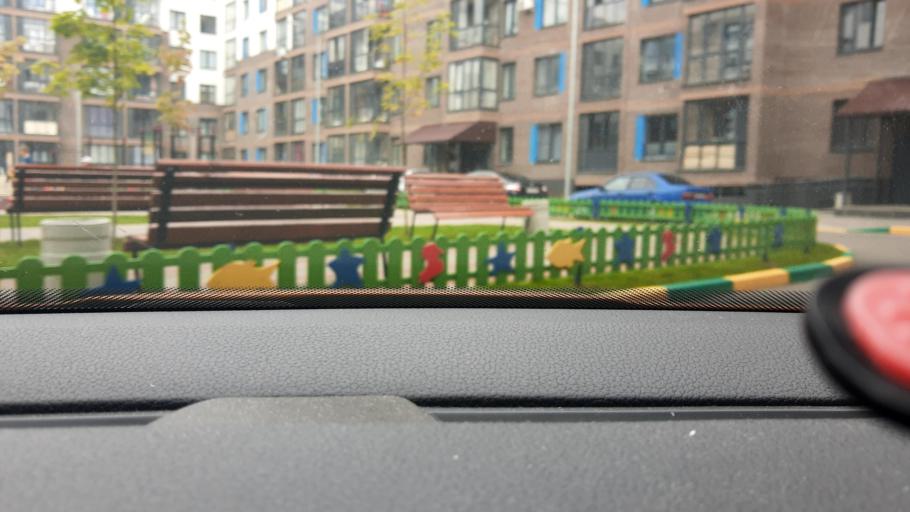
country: RU
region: Moskovskaya
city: Pirogovskiy
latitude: 55.9576
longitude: 37.6847
